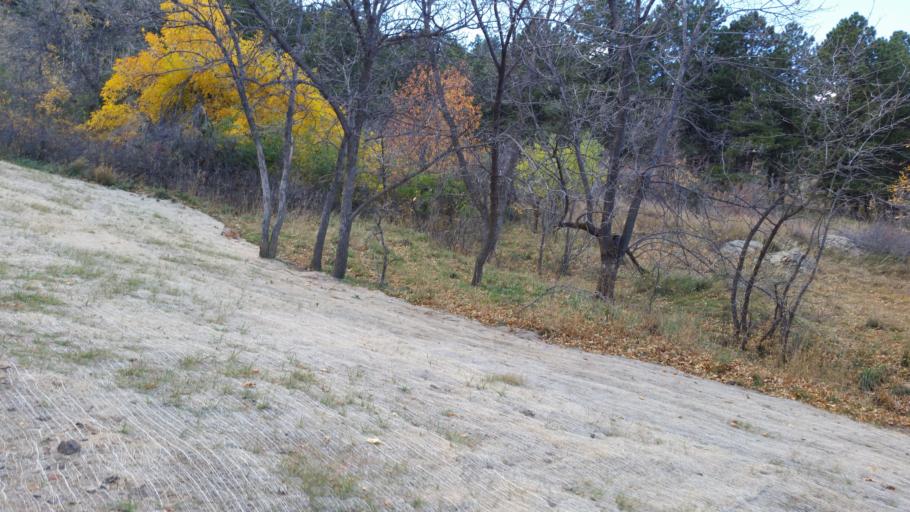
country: US
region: Colorado
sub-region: Boulder County
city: Boulder
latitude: 39.9952
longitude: -105.2868
